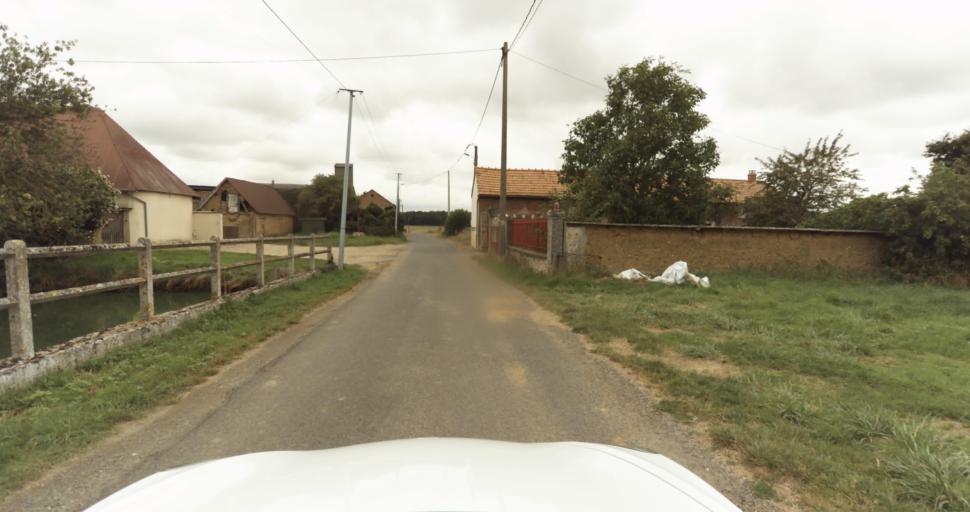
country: FR
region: Haute-Normandie
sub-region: Departement de l'Eure
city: Saint-Sebastien-de-Morsent
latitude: 49.0177
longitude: 1.0613
